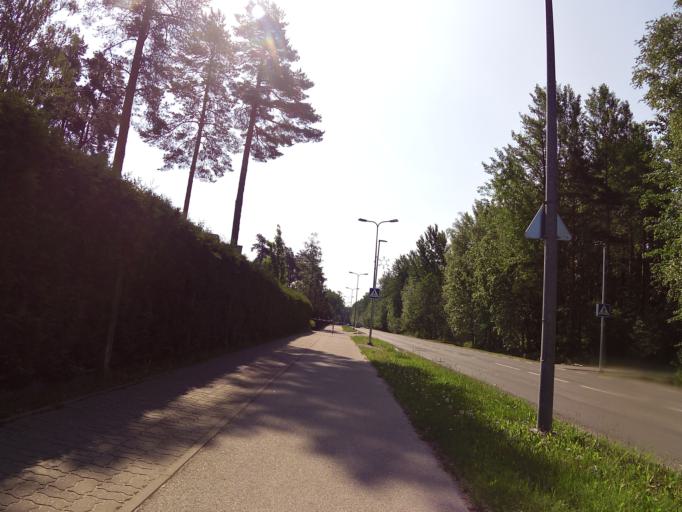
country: EE
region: Harju
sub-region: Harku vald
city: Tabasalu
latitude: 59.4417
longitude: 24.6197
